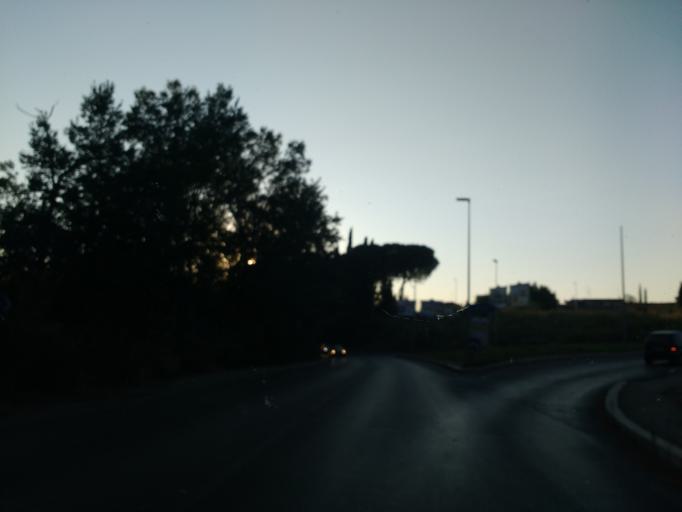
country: IT
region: Latium
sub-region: Citta metropolitana di Roma Capitale
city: Villanova
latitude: 41.9564
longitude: 12.7620
